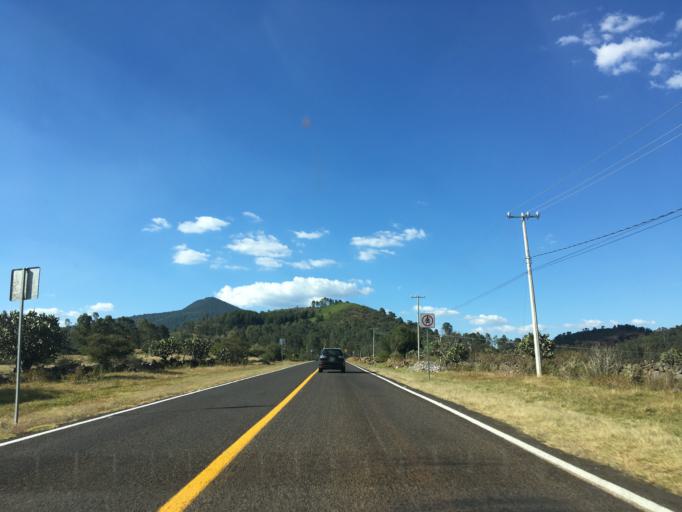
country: MX
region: Michoacan
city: Tzintzuntzan
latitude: 19.5814
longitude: -101.5771
